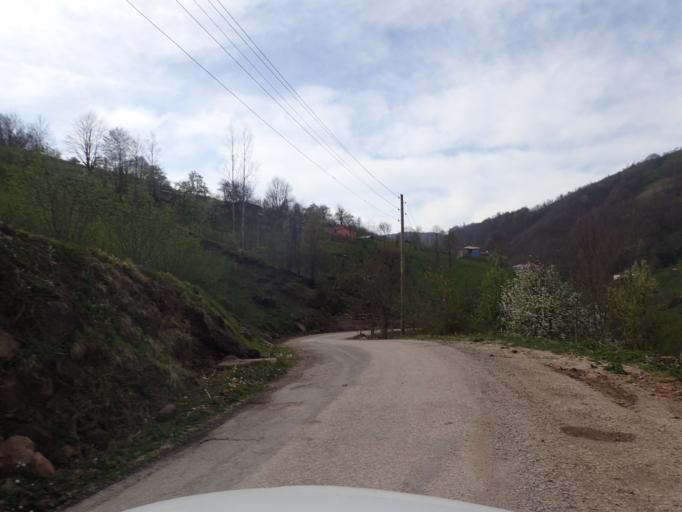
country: TR
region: Ordu
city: Aybasti
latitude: 40.7006
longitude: 37.2808
